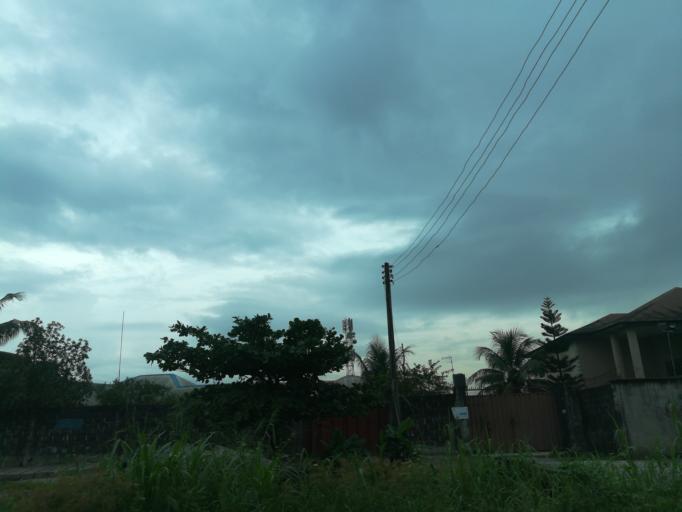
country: NG
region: Rivers
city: Port Harcourt
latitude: 4.8178
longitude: 7.0160
